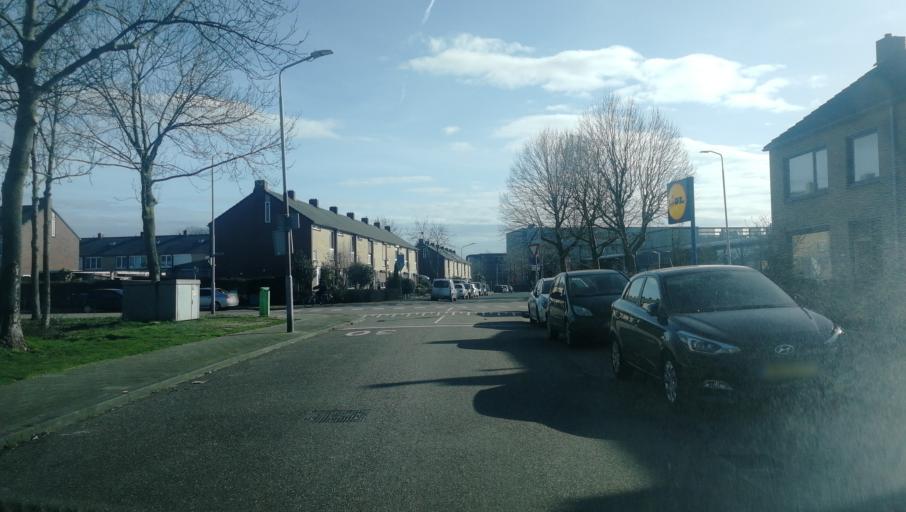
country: NL
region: Limburg
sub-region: Gemeente Venlo
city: Venlo
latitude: 51.3589
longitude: 6.1606
